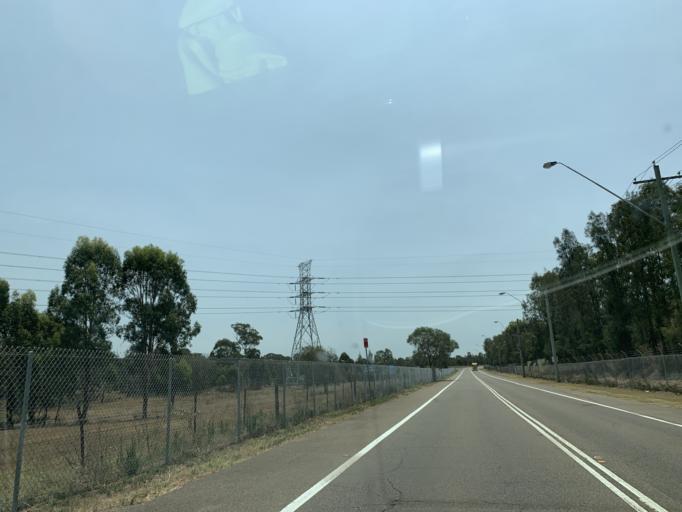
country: AU
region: New South Wales
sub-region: Fairfield
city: Horsley Park
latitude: -33.8064
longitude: 150.8641
